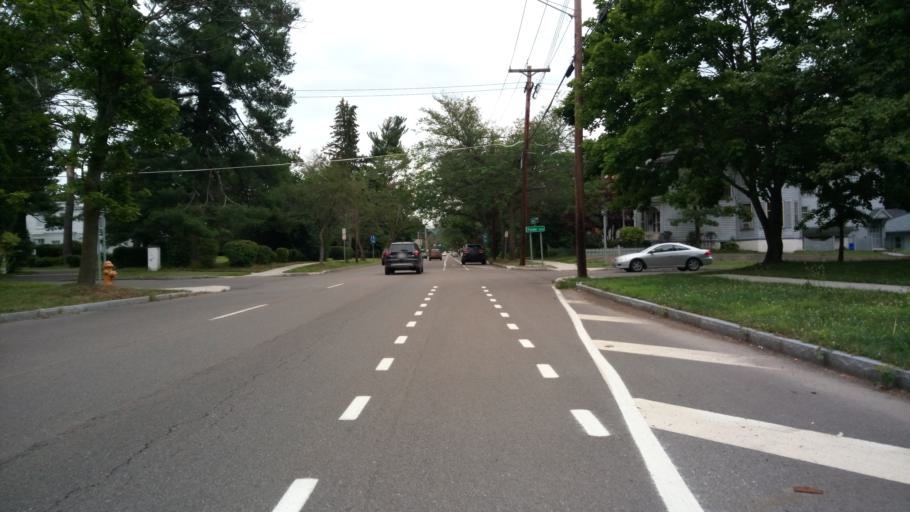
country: US
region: New York
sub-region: Chemung County
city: Elmira
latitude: 42.0825
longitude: -76.8255
